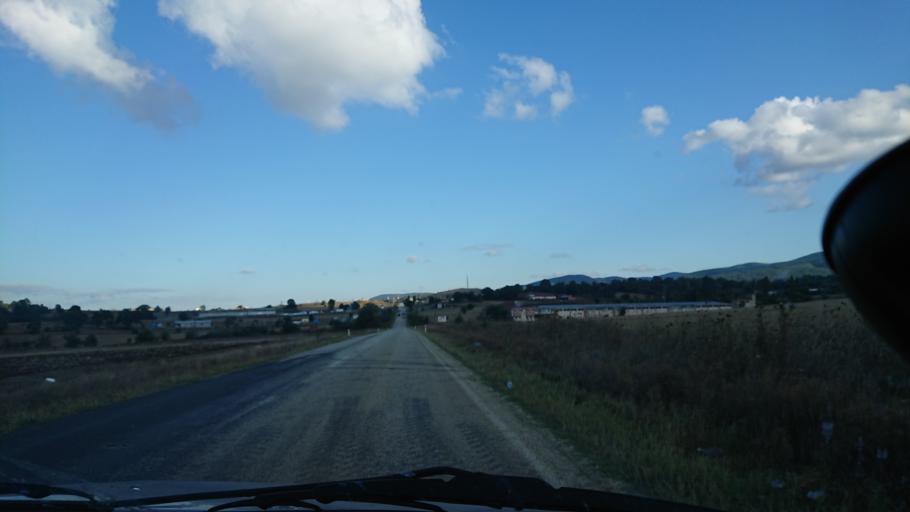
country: TR
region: Bilecik
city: Pazaryeri
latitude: 40.0054
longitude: 29.8771
